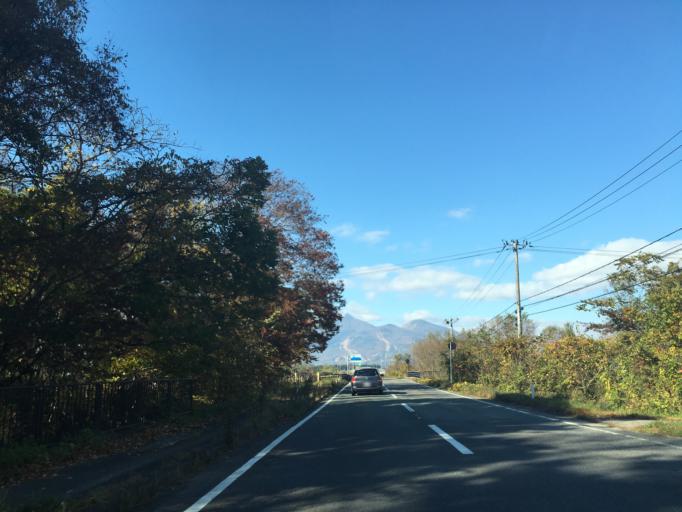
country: JP
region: Fukushima
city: Inawashiro
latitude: 37.5051
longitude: 140.1441
